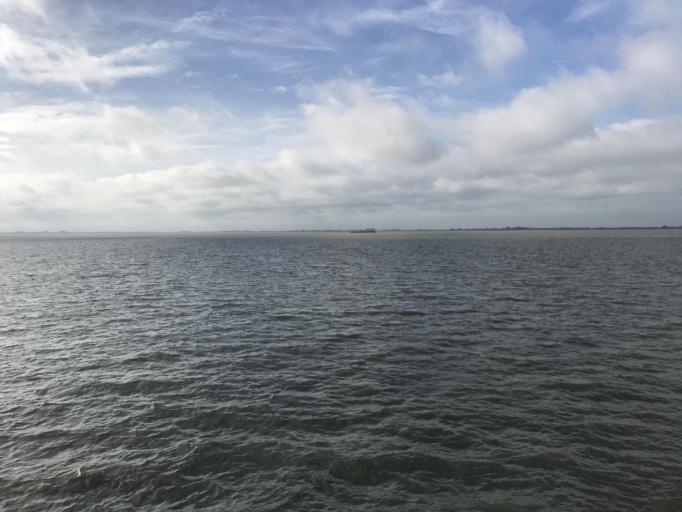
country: NL
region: Groningen
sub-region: Gemeente Delfzijl
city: Delfzijl
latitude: 53.4121
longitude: 6.9399
